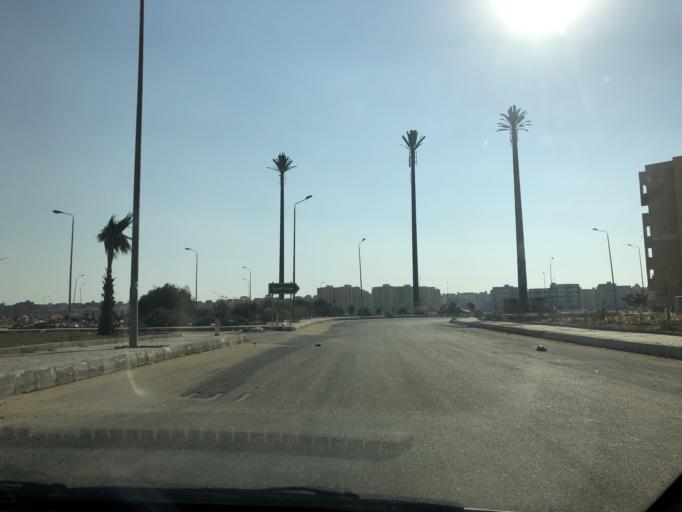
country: EG
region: Al Jizah
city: Madinat Sittah Uktubar
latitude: 29.9185
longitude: 31.0646
